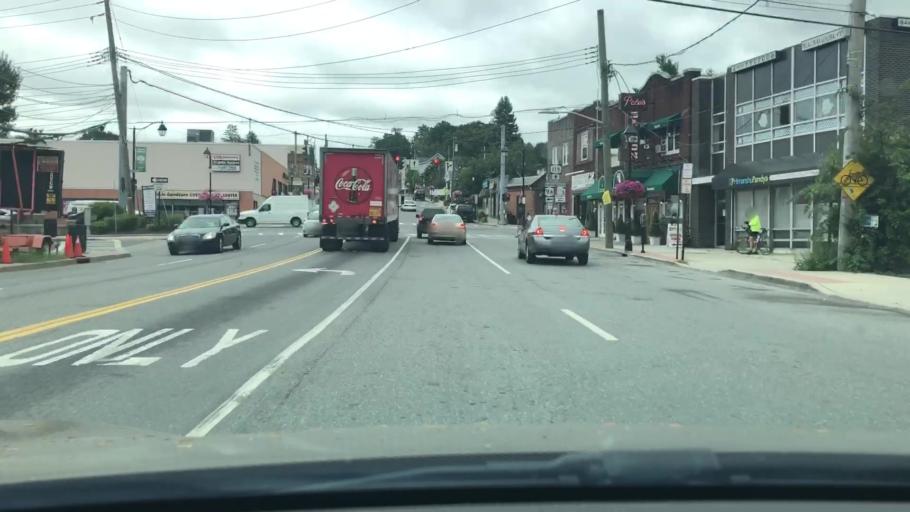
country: US
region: New York
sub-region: Westchester County
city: Elmsford
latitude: 41.0552
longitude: -73.8206
